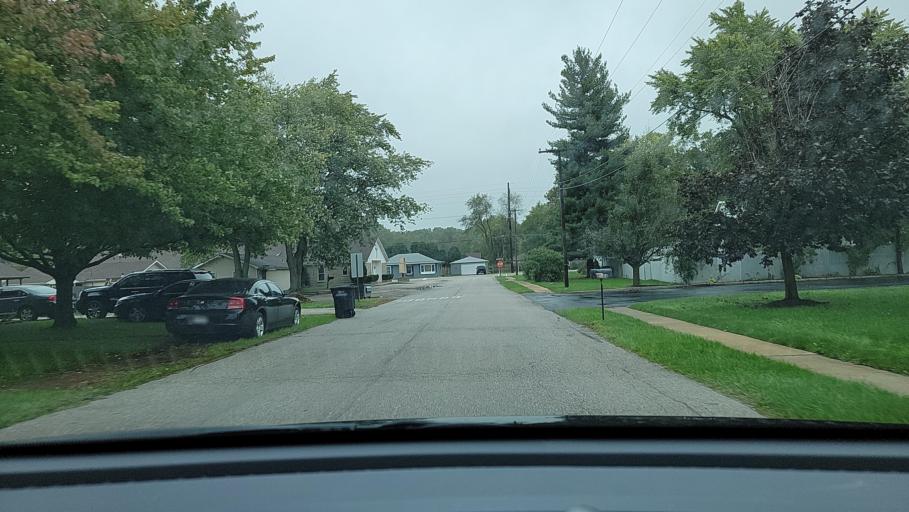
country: US
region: Indiana
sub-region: Porter County
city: Portage
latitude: 41.5708
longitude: -87.1895
